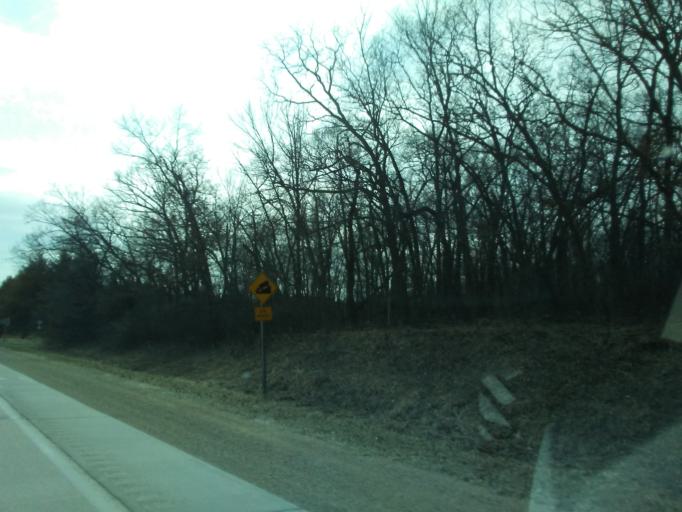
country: US
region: Iowa
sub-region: Winneshiek County
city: Decorah
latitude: 43.3377
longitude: -91.8121
